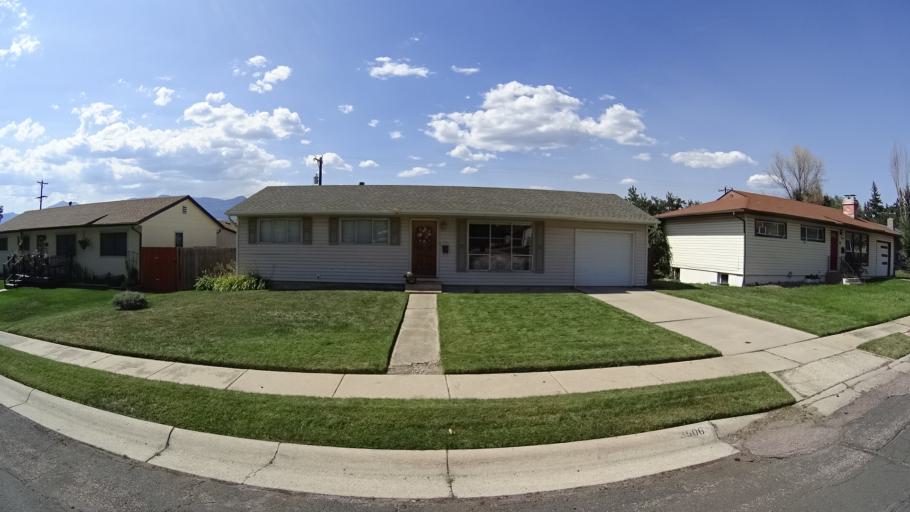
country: US
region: Colorado
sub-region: El Paso County
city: Colorado Springs
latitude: 38.8844
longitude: -104.8082
